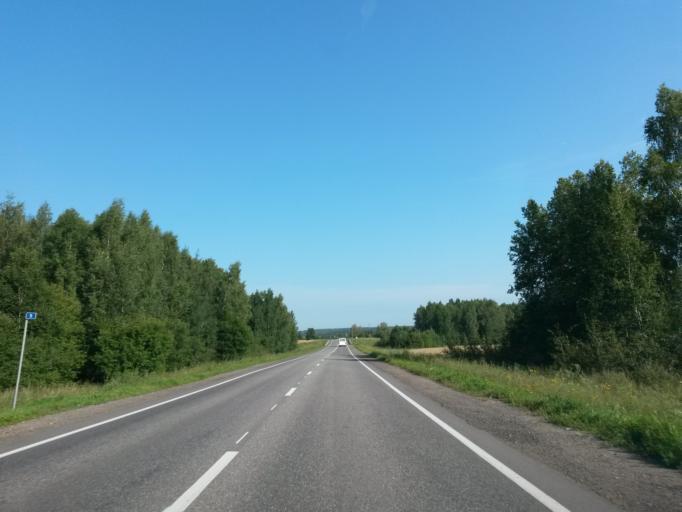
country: RU
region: Jaroslavl
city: Gavrilov-Yam
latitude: 57.3165
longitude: 39.9335
